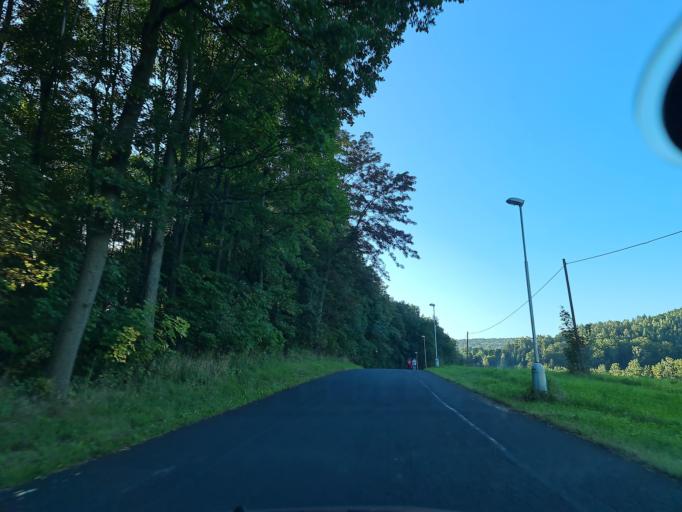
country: DE
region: Saxony
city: Olbernhau
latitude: 50.6461
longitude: 13.3752
